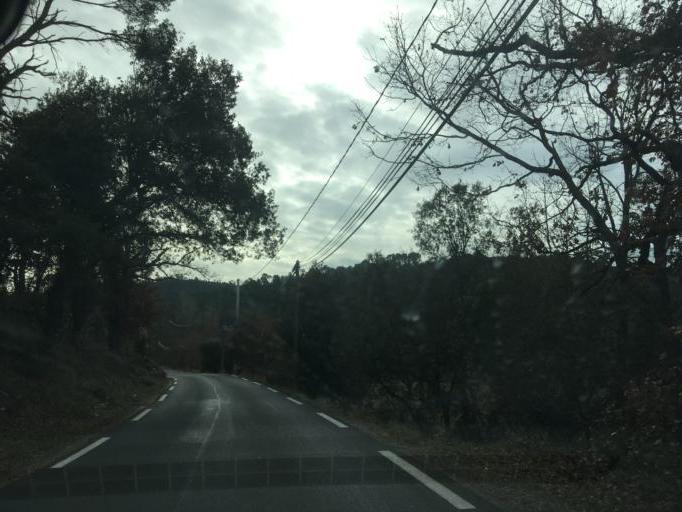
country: FR
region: Provence-Alpes-Cote d'Azur
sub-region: Departement du Var
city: Bras
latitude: 43.4631
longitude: 5.9639
